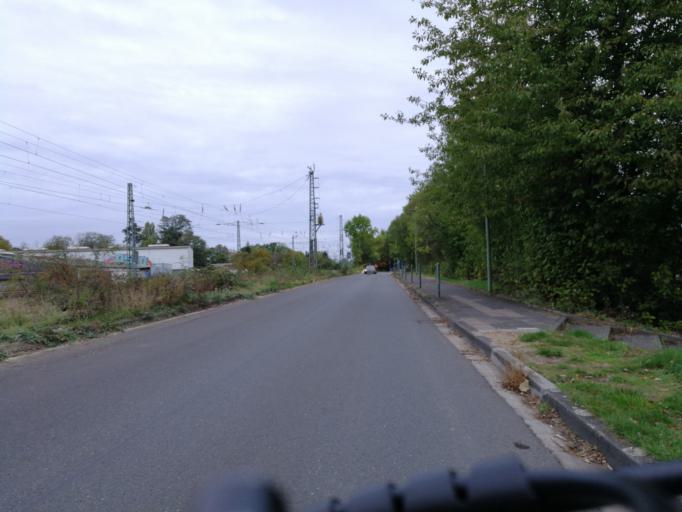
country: DE
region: North Rhine-Westphalia
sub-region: Regierungsbezirk Dusseldorf
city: Neuss
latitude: 51.1549
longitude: 6.7403
